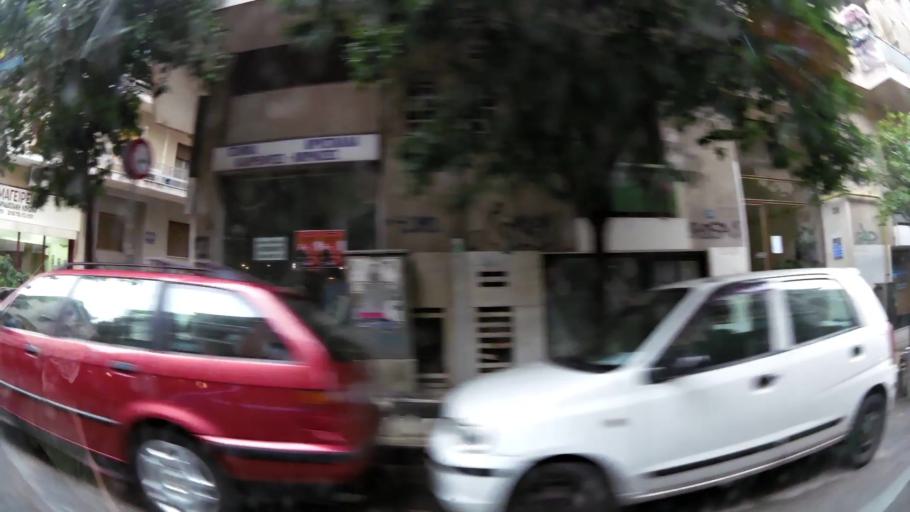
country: GR
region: Attica
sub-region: Nomarchia Athinas
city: Vyronas
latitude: 37.9677
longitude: 23.7522
